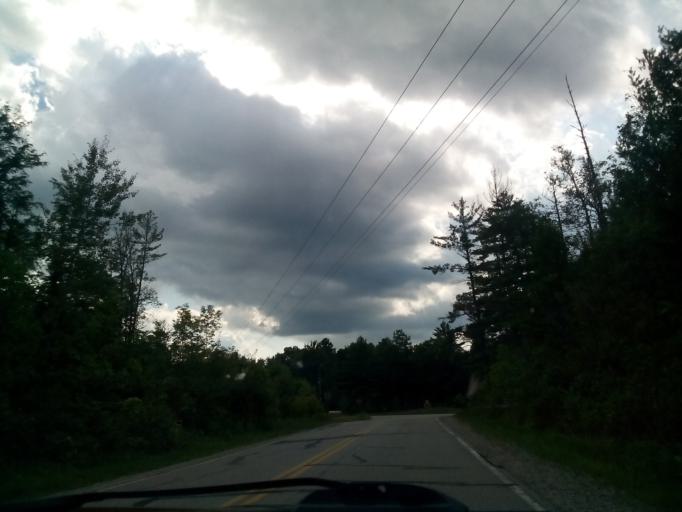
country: US
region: Wisconsin
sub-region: Marinette County
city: Niagara
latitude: 45.4953
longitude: -87.9832
